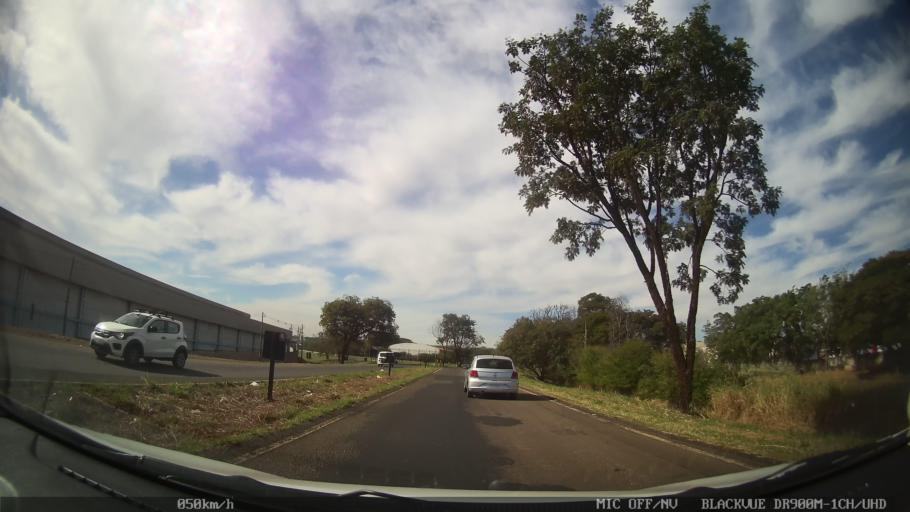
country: BR
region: Sao Paulo
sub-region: Araraquara
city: Araraquara
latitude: -21.8340
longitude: -48.1539
